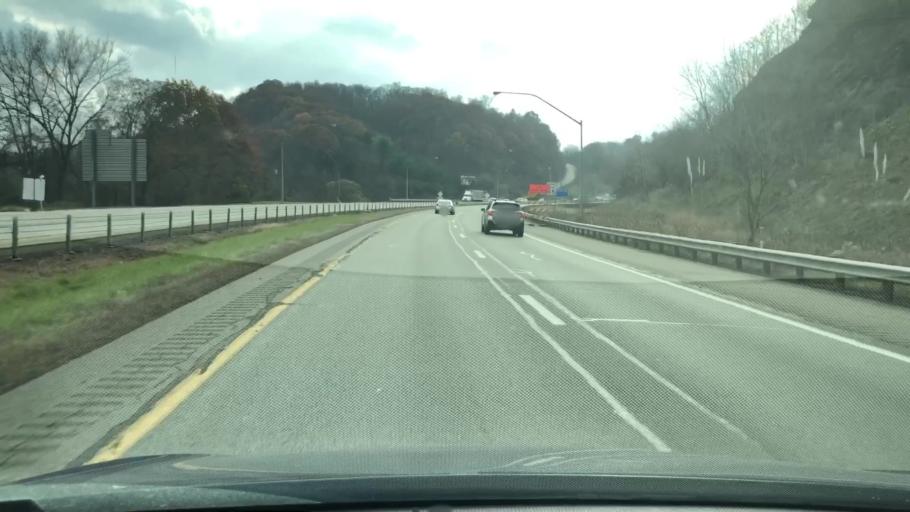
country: US
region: Pennsylvania
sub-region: Westmoreland County
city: Arnold
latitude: 40.5847
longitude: -79.7791
